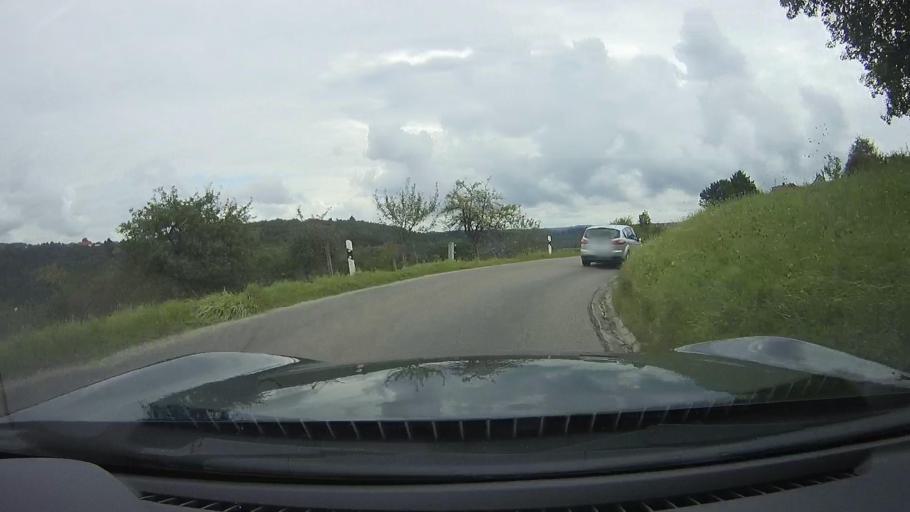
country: DE
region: Baden-Wuerttemberg
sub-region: Regierungsbezirk Stuttgart
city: Murrhardt
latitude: 49.0015
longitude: 9.5682
